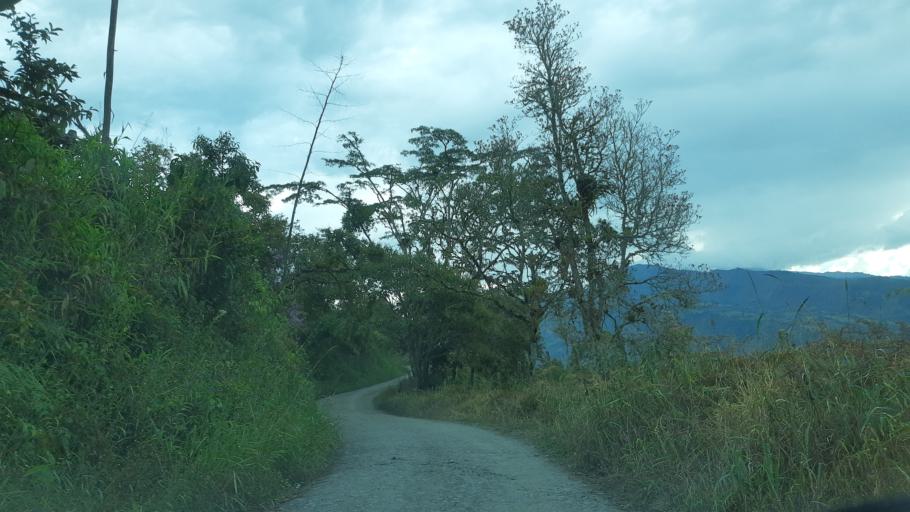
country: CO
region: Boyaca
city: Garagoa
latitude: 4.9853
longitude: -73.3232
